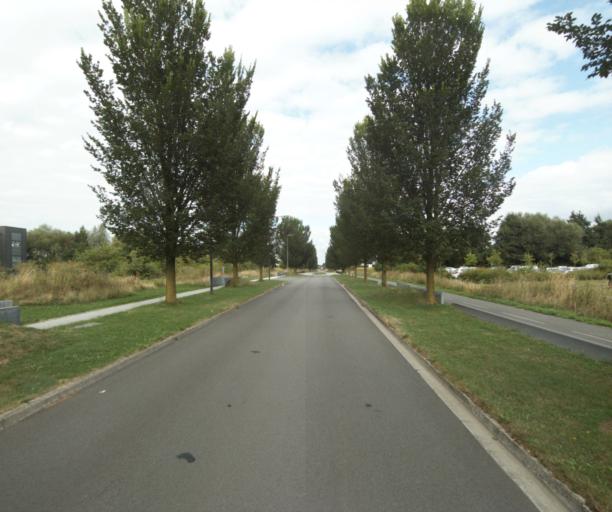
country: FR
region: Nord-Pas-de-Calais
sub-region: Departement du Nord
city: Villeneuve-d'Ascq
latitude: 50.6060
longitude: 3.1507
